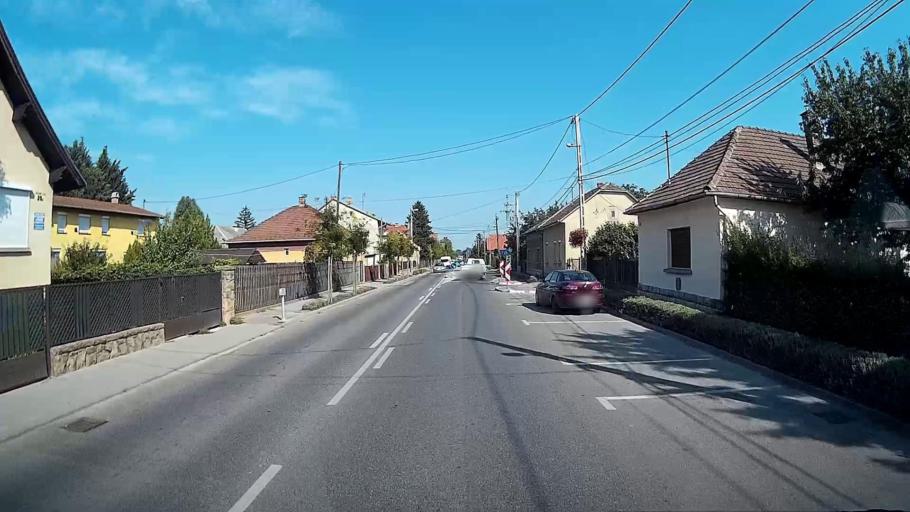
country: HU
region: Pest
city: Budakalasz
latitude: 47.6217
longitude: 19.0539
